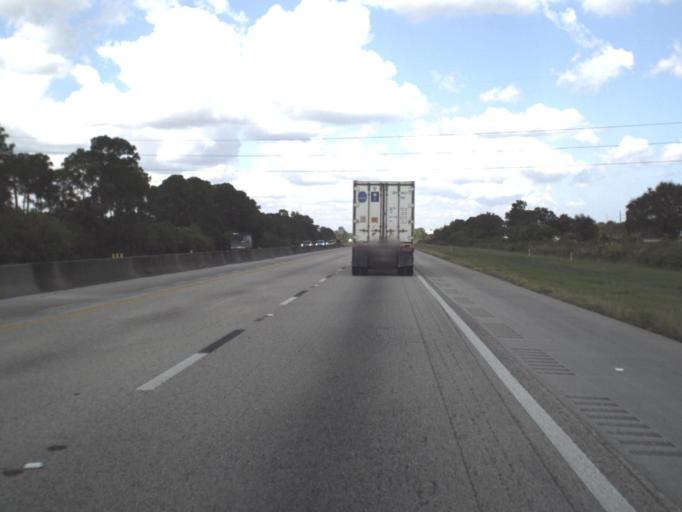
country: US
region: Florida
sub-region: Martin County
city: Port Salerno
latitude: 27.0867
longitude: -80.2533
